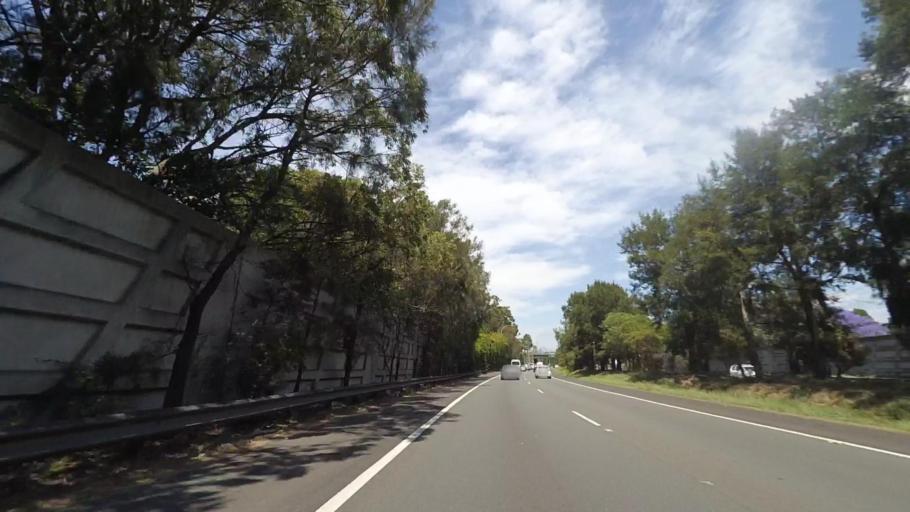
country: AU
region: New South Wales
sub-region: Wollongong
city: Mangerton
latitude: -34.4368
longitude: 150.8680
